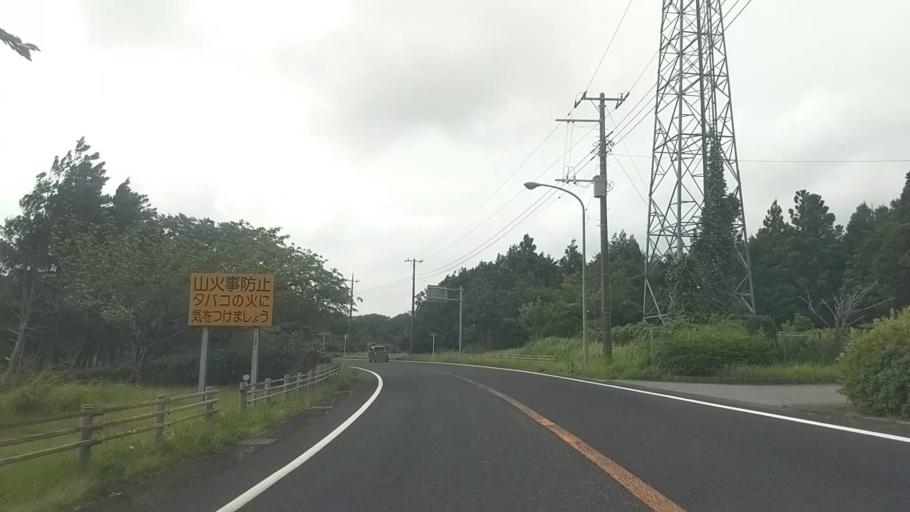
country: JP
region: Chiba
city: Kawaguchi
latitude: 35.2295
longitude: 140.0314
